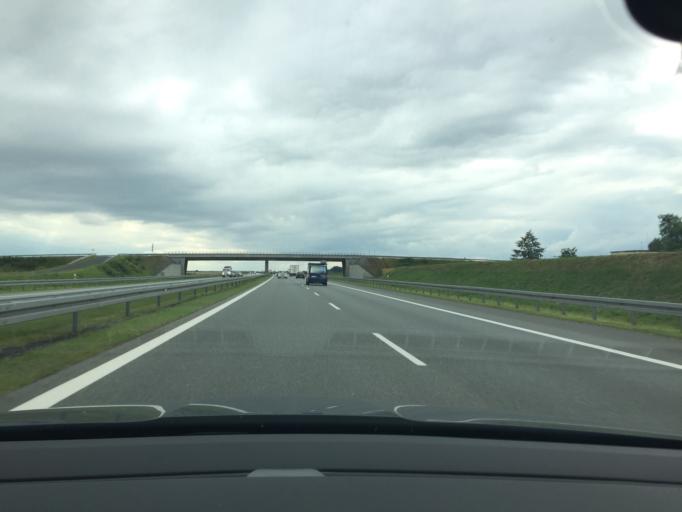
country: PL
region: Greater Poland Voivodeship
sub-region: Powiat szamotulski
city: Duszniki
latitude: 52.3896
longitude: 16.4311
